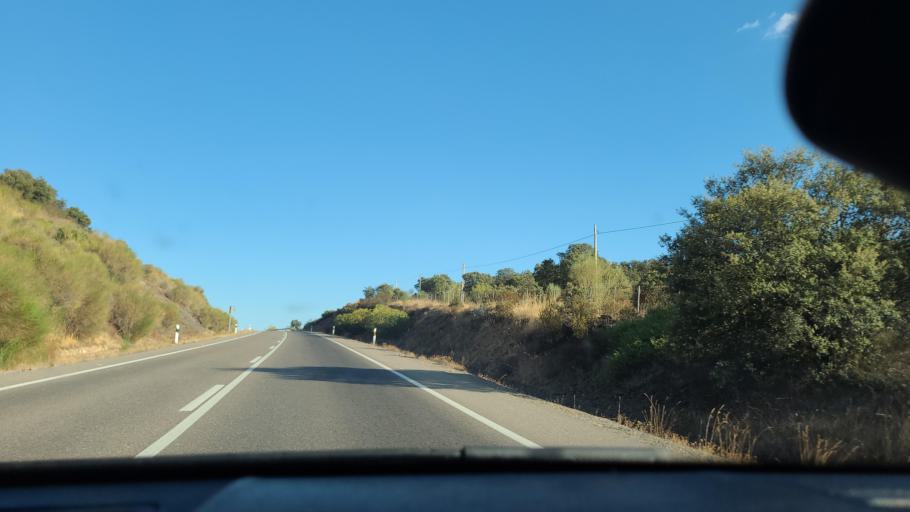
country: ES
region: Andalusia
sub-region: Province of Cordoba
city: Espiel
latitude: 38.1945
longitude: -5.0986
